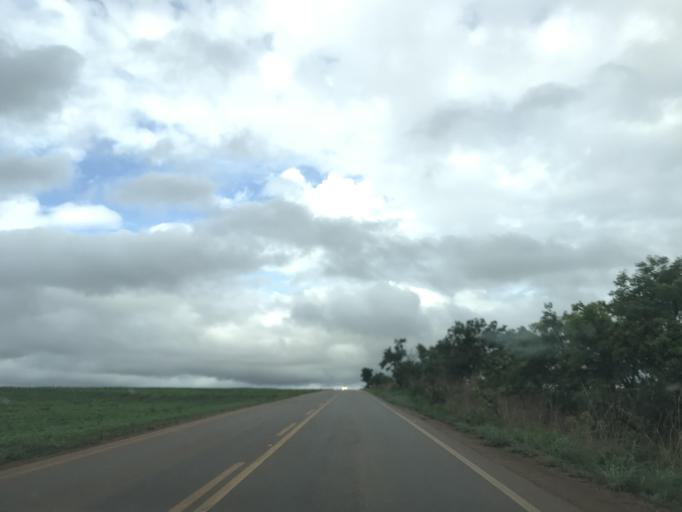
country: BR
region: Goias
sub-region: Vianopolis
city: Vianopolis
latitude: -16.5599
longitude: -48.2824
